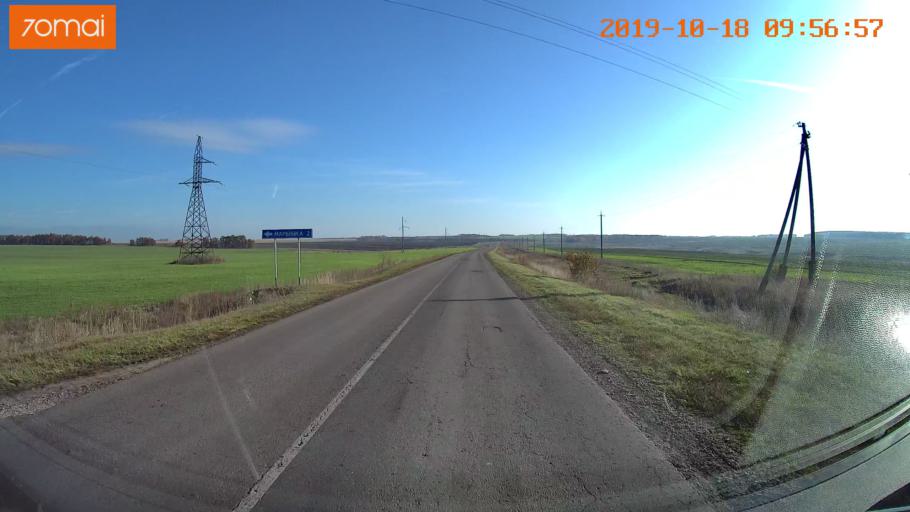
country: RU
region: Tula
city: Kurkino
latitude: 53.3757
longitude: 38.4031
